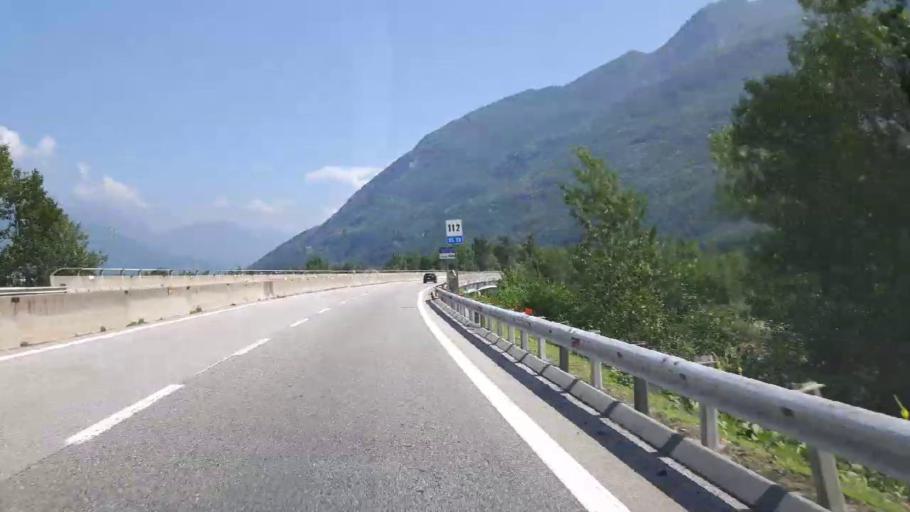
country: IT
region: Piedmont
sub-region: Provincia Verbano-Cusio-Ossola
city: Pieve Vergonte
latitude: 46.0197
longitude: 8.2753
